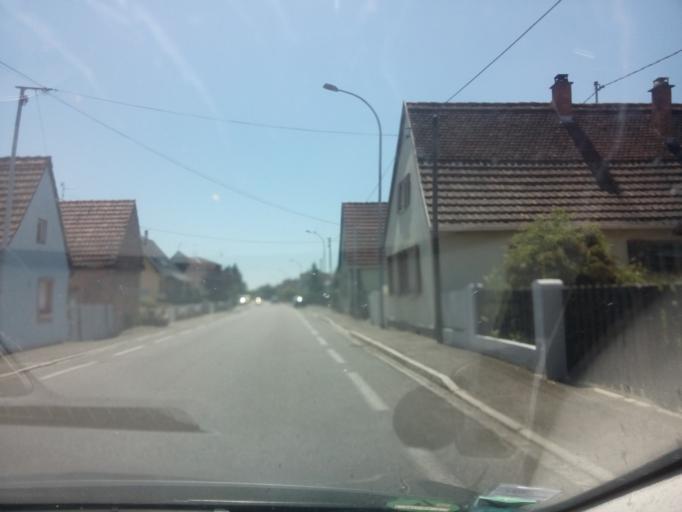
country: FR
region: Alsace
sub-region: Departement du Bas-Rhin
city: Kaltenhouse
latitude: 48.7887
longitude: 7.8355
